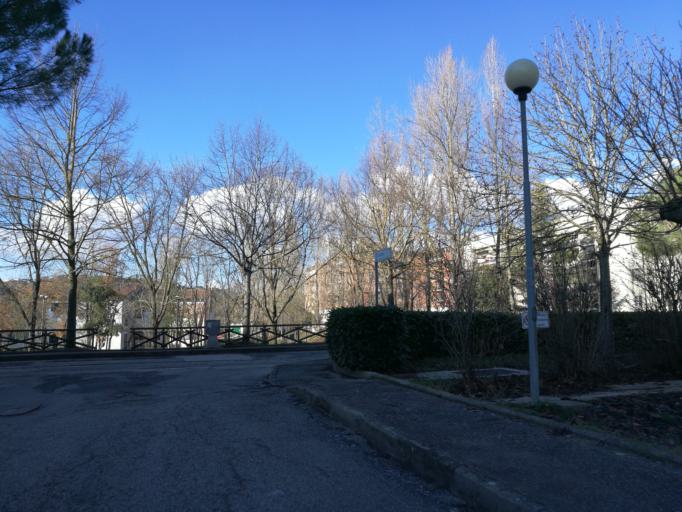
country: IT
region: Umbria
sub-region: Provincia di Perugia
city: Perugia
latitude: 43.0788
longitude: 12.3681
